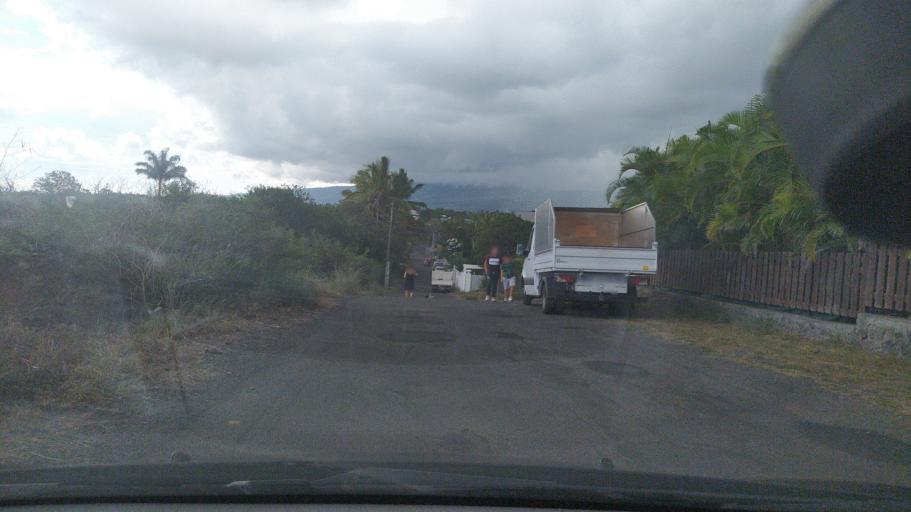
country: RE
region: Reunion
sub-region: Reunion
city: Saint-Pierre
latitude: -21.3020
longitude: 55.4616
